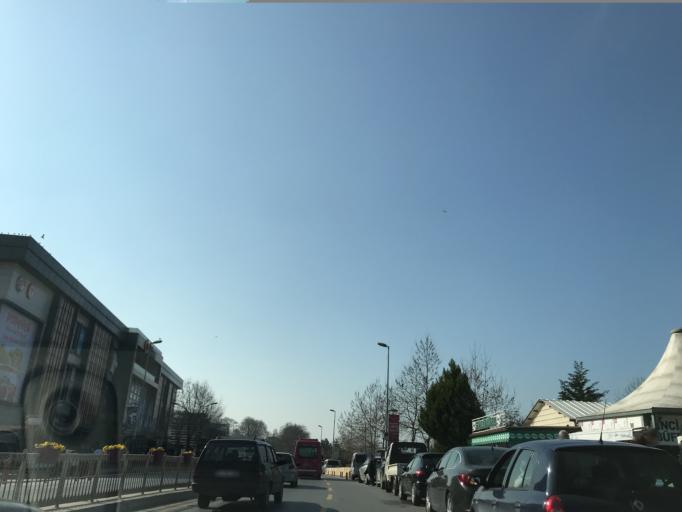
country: TR
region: Yalova
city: Yalova
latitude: 40.6592
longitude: 29.2785
